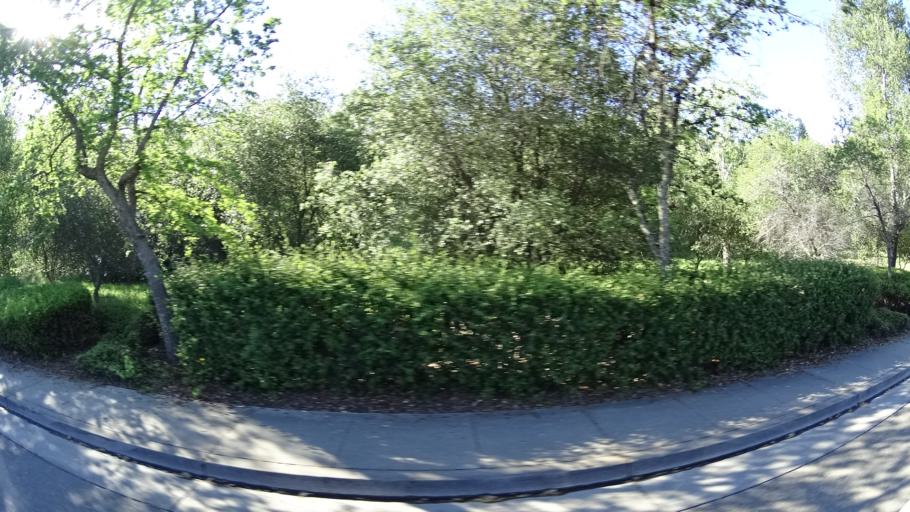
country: US
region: California
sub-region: Placer County
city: Loomis
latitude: 38.8378
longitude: -121.2368
